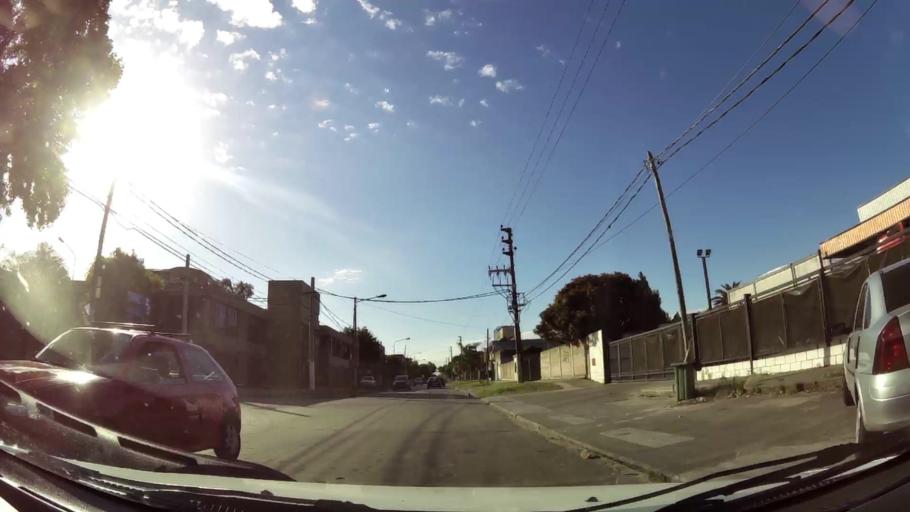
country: AR
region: Buenos Aires
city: Caseros
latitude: -34.5744
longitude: -58.5980
